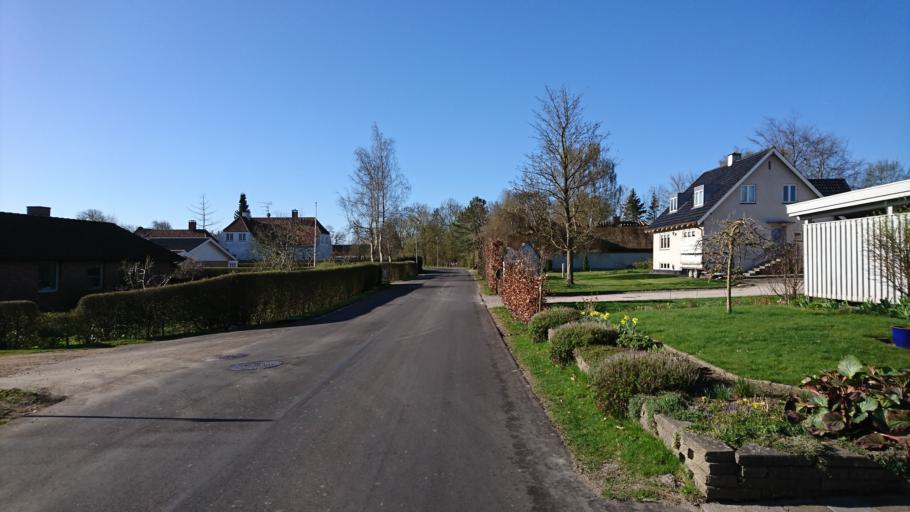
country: DK
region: Capital Region
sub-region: Frederikssund Kommune
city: Skibby
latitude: 55.7256
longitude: 11.9292
